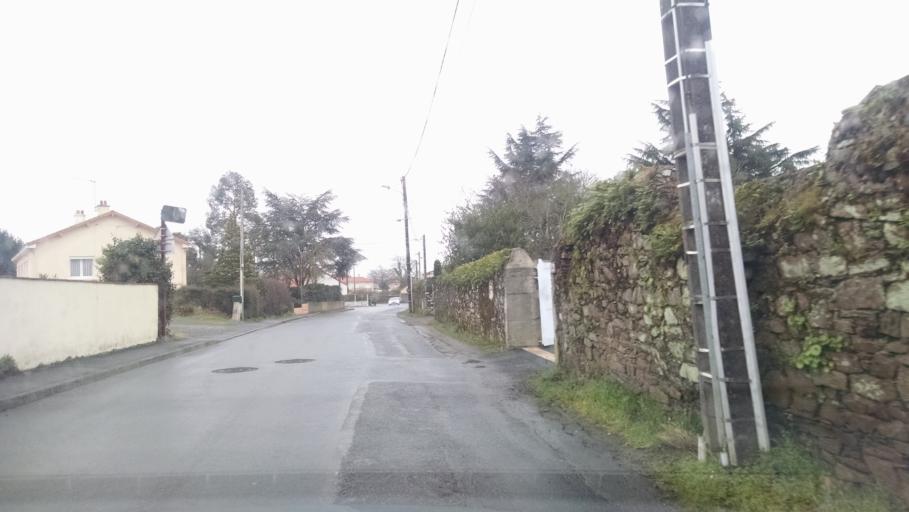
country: FR
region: Pays de la Loire
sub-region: Departement de la Loire-Atlantique
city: Clisson
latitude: 47.0900
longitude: -1.2746
